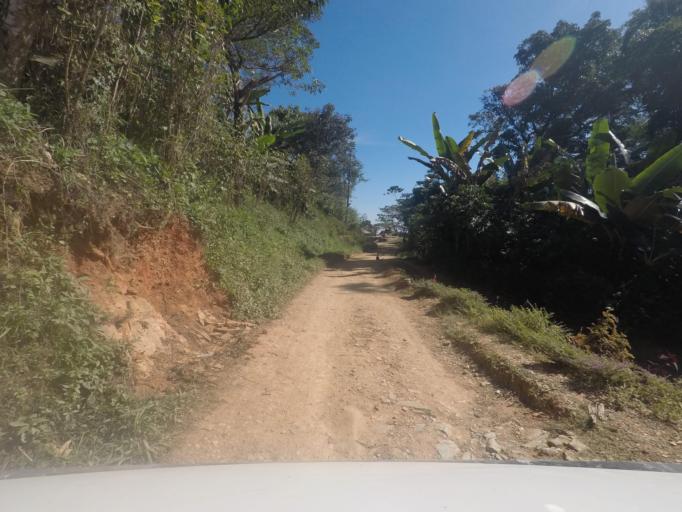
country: TL
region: Ermera
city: Gleno
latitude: -8.7342
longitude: 125.3435
